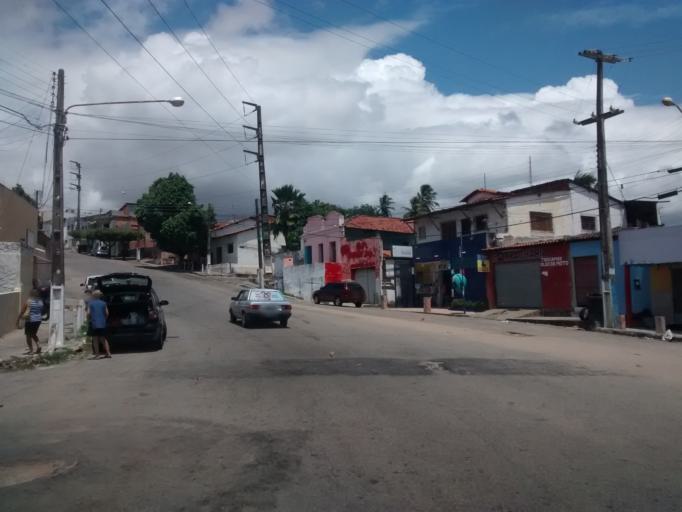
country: BR
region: Rio Grande do Norte
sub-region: Natal
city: Natal
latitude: -5.7897
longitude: -35.2127
